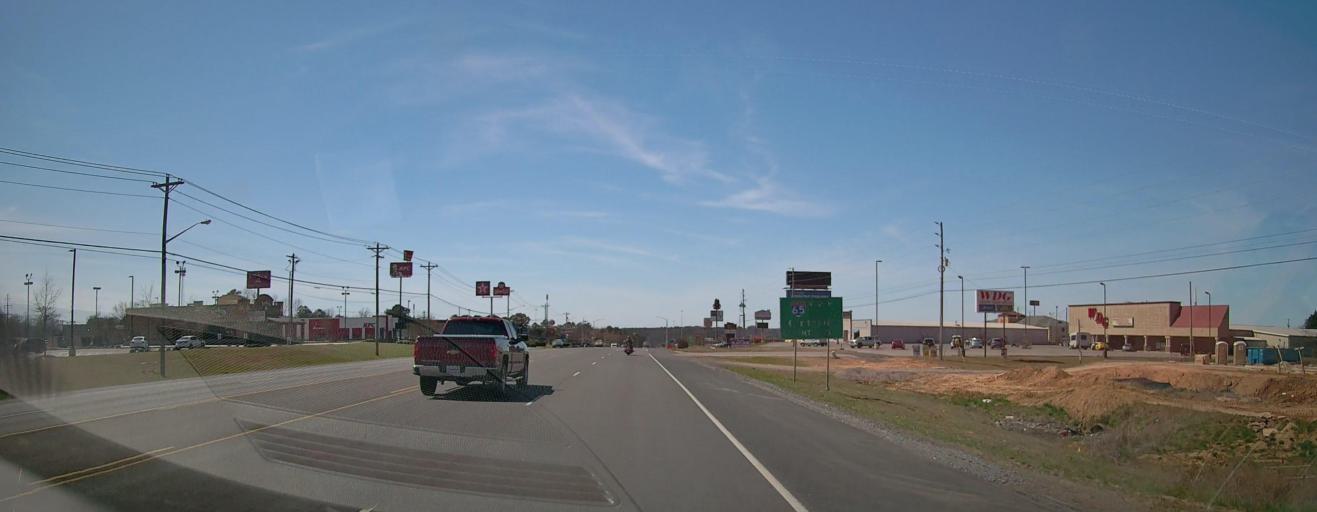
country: US
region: Alabama
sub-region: Cullman County
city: Cullman
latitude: 34.2067
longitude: -86.8698
